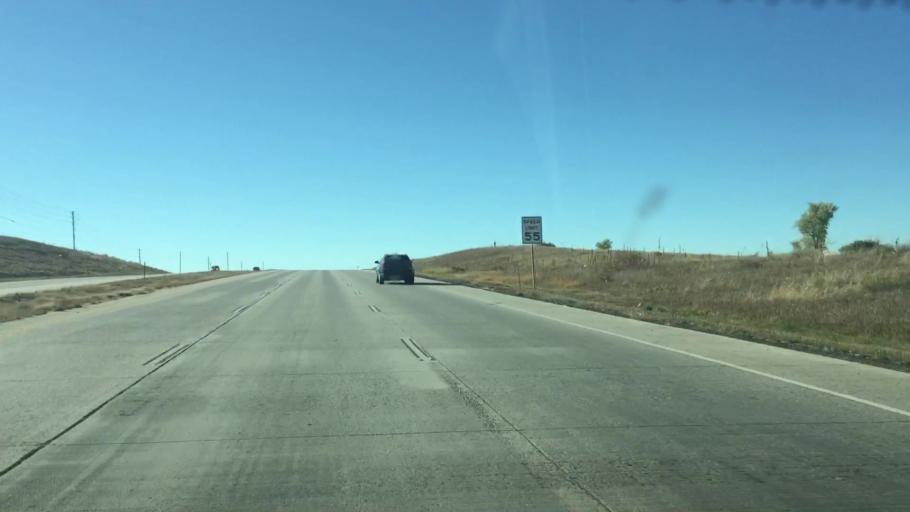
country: US
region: Colorado
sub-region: Douglas County
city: The Pinery
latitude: 39.4731
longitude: -104.7585
